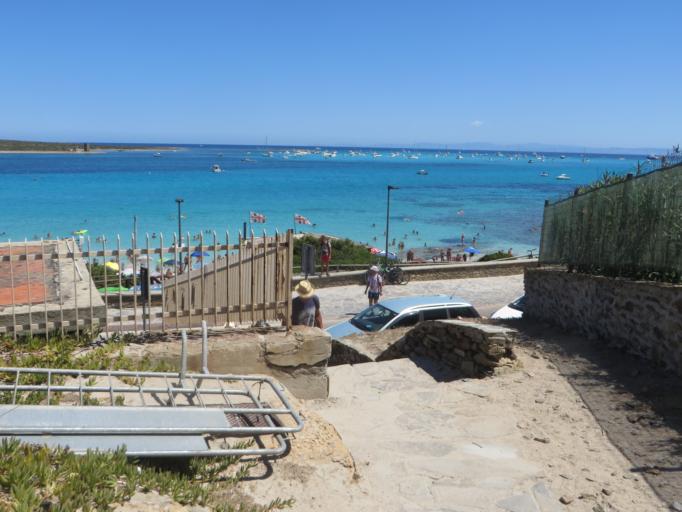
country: IT
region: Sardinia
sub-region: Provincia di Sassari
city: Stintino
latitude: 40.9646
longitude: 8.2091
